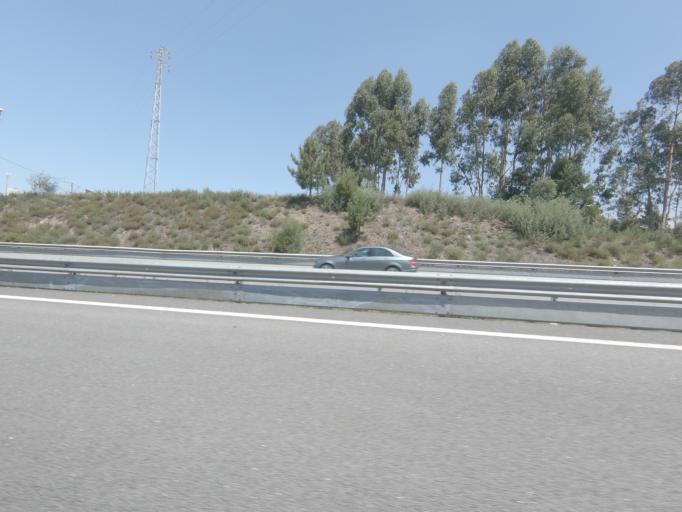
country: PT
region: Porto
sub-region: Gondomar
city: Baguim do Monte
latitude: 41.2031
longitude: -8.5266
